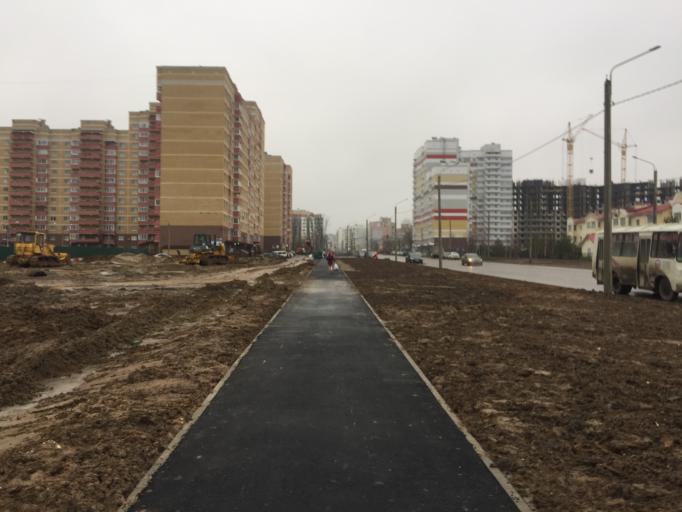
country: RU
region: Jaroslavl
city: Yaroslavl
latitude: 57.7000
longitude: 39.7907
